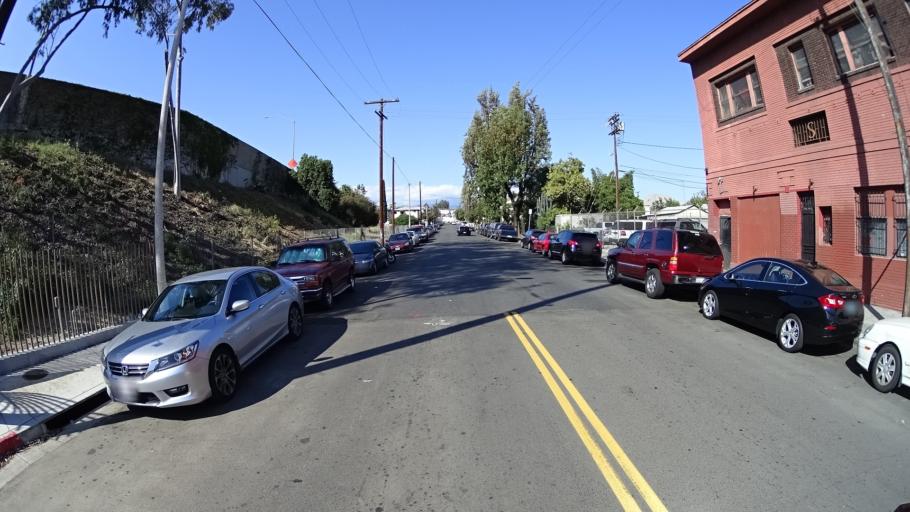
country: US
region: California
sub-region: Los Angeles County
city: Boyle Heights
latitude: 34.0456
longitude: -118.2149
